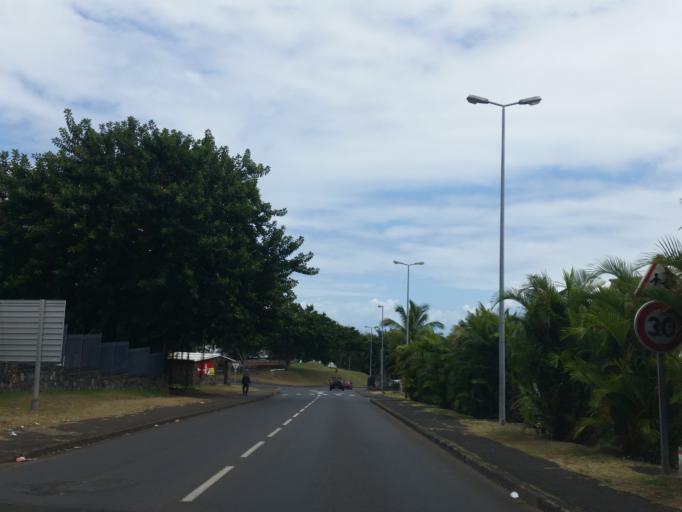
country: RE
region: Reunion
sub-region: Reunion
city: Saint-Denis
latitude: -20.8993
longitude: 55.4870
